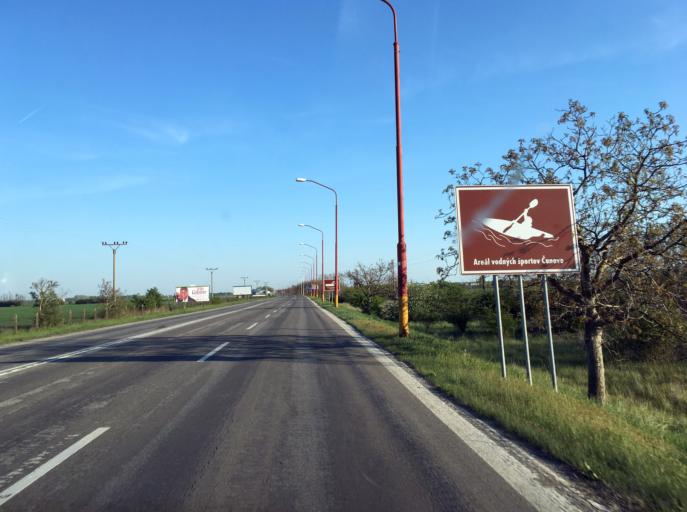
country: HU
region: Gyor-Moson-Sopron
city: Rajka
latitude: 48.0287
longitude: 17.1685
